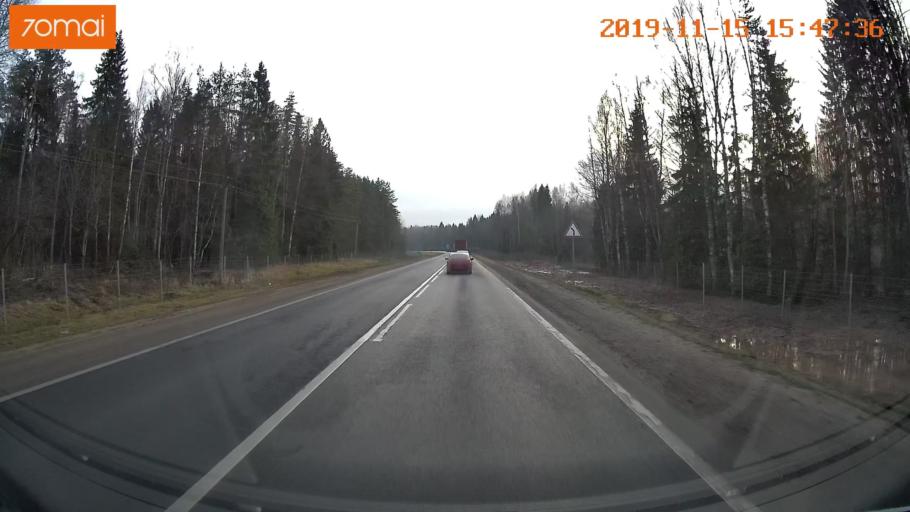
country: RU
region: Jaroslavl
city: Danilov
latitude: 57.9365
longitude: 40.0085
